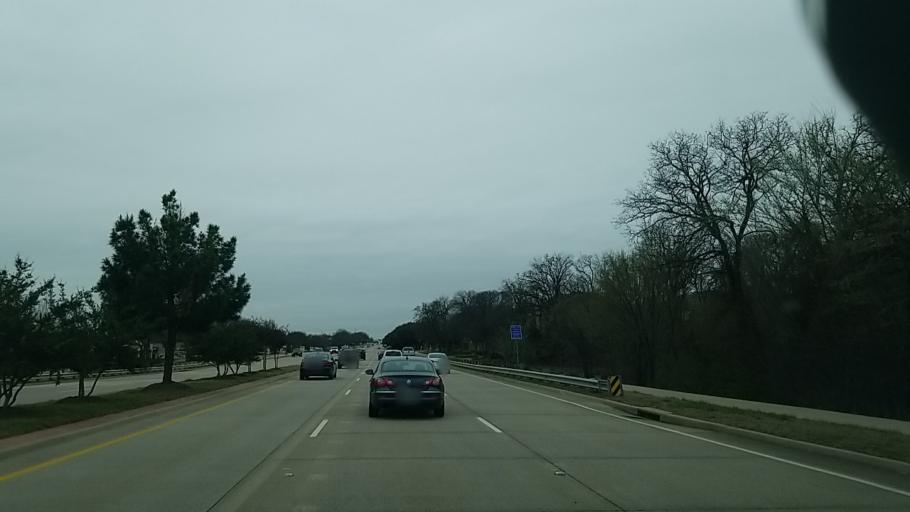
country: US
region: Texas
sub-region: Denton County
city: Flower Mound
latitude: 33.0234
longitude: -97.0709
